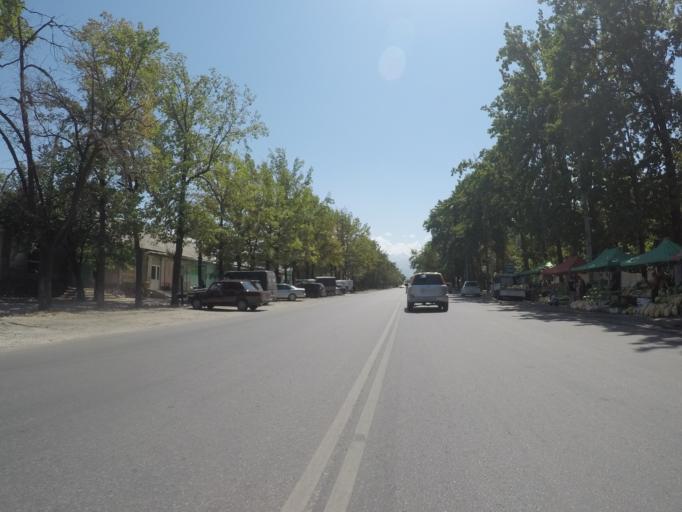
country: KG
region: Chuy
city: Bishkek
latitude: 42.8479
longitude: 74.5769
